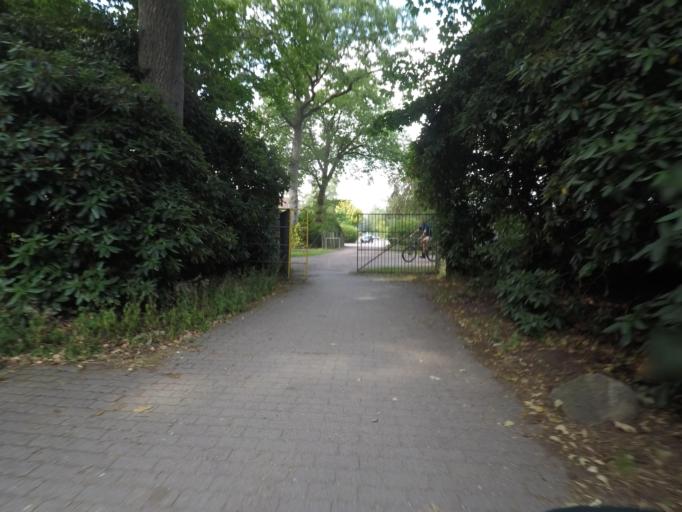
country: DE
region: Hamburg
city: Wellingsbuettel
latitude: 53.6300
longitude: 10.0690
